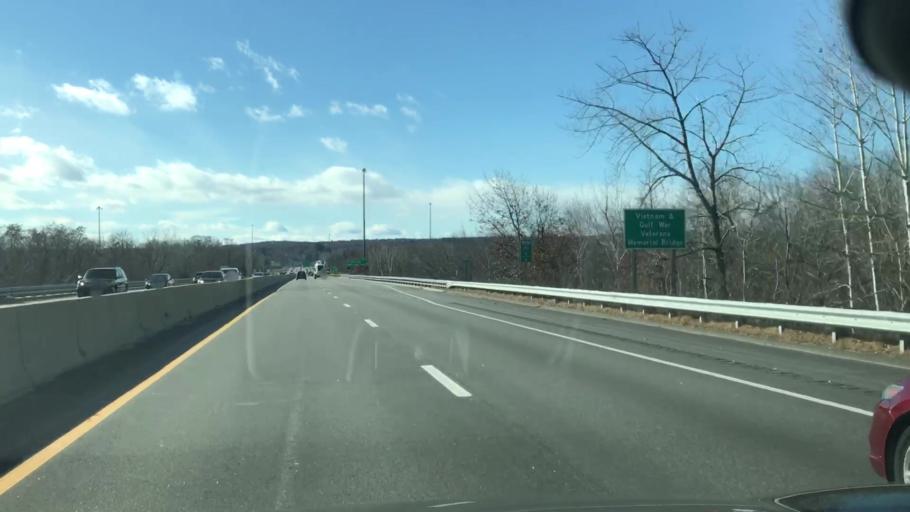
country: US
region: New Hampshire
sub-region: Merrimack County
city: Concord
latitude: 43.2200
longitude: -71.5218
